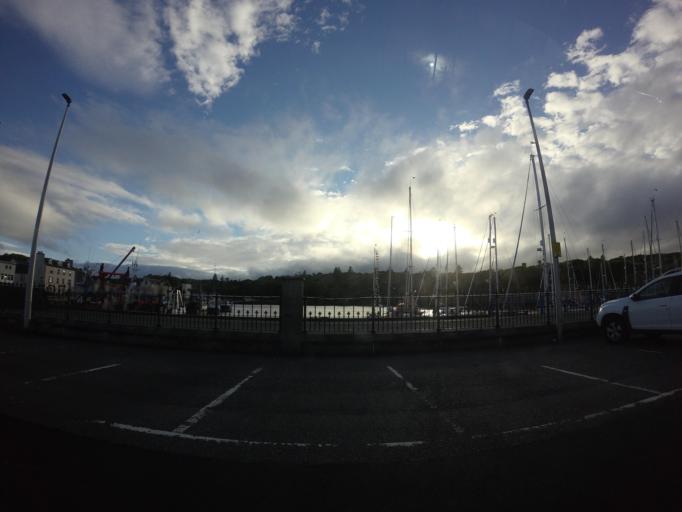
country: GB
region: Scotland
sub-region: Eilean Siar
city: Stornoway
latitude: 58.2091
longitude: -6.3893
